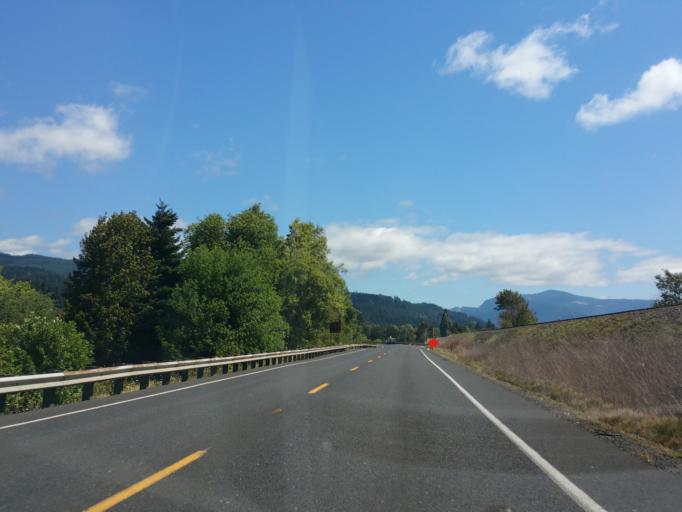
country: US
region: Washington
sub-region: Skamania County
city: Stevenson
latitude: 45.6866
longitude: -121.8937
